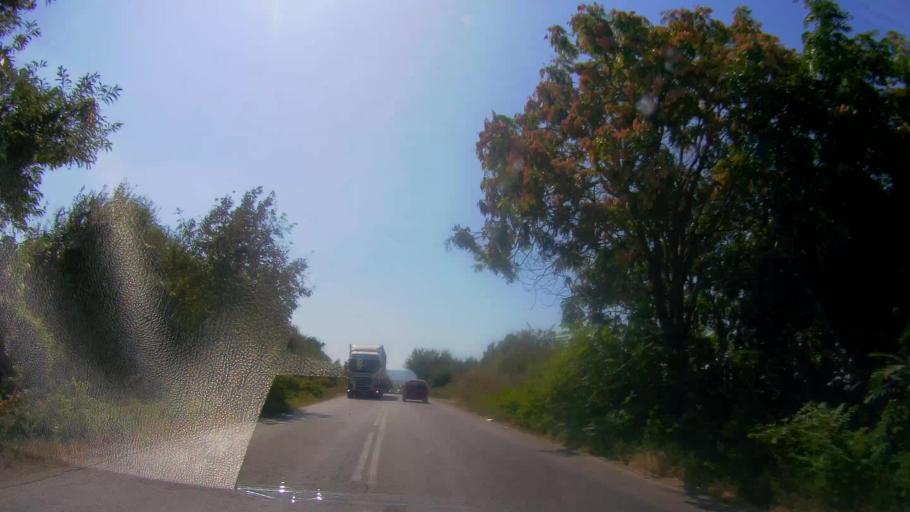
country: BG
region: Veliko Turnovo
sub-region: Obshtina Gorna Oryakhovitsa
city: Purvomaytsi
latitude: 43.2321
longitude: 25.6403
